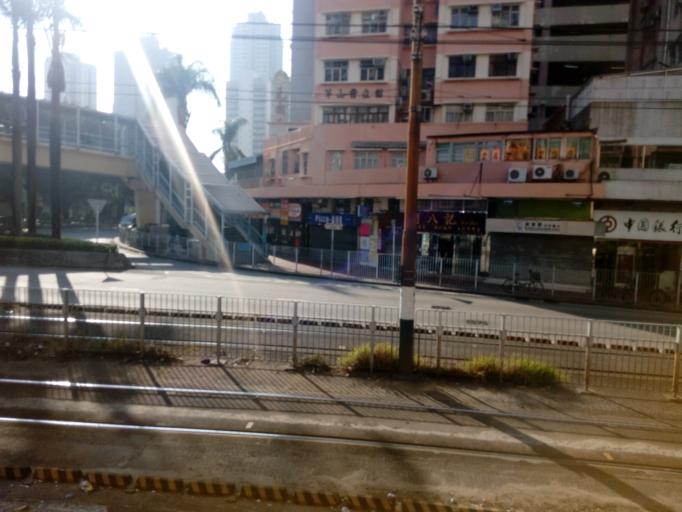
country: HK
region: Yuen Long
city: Yuen Long Kau Hui
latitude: 22.4441
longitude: 114.0317
